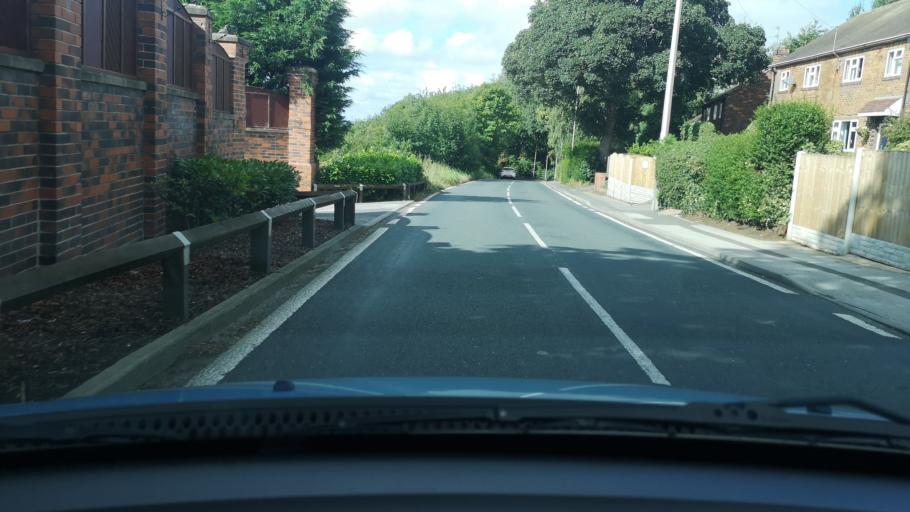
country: GB
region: England
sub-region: City and Borough of Wakefield
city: Featherstone
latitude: 53.6931
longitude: -1.3643
